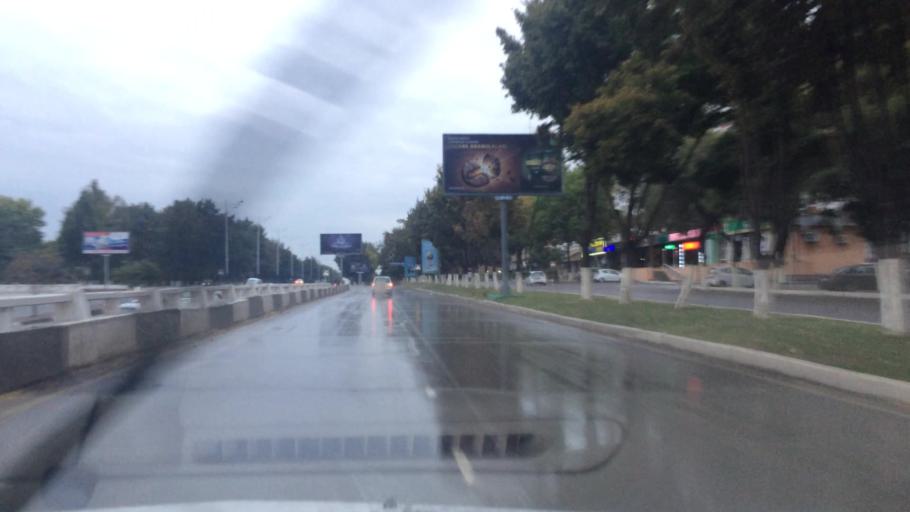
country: UZ
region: Toshkent Shahri
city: Tashkent
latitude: 41.3092
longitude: 69.2389
